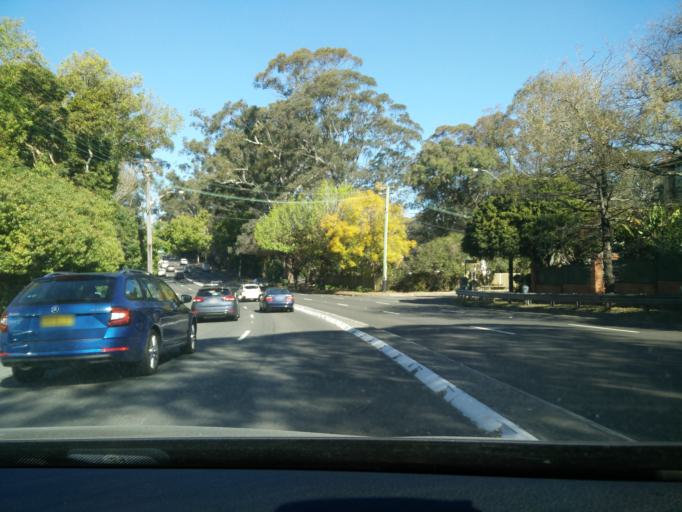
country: AU
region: New South Wales
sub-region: City of Sydney
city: Pymble
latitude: -33.7365
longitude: 151.1332
